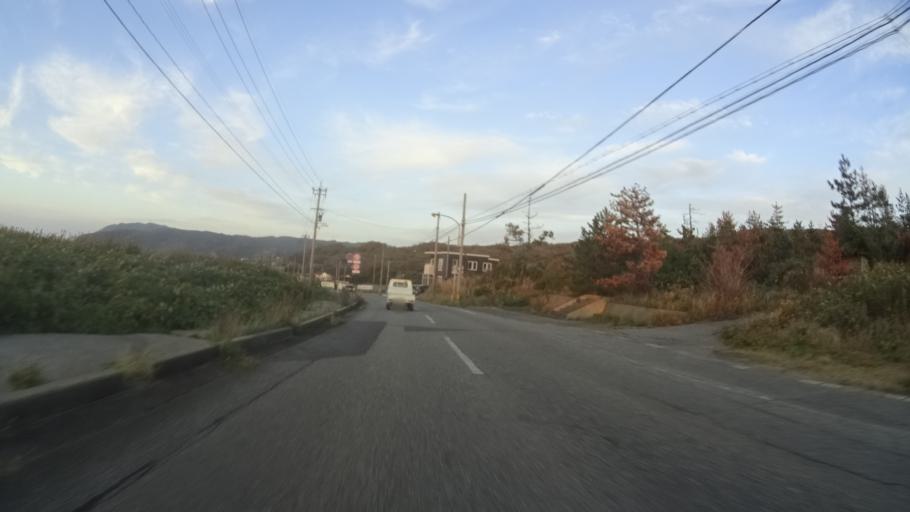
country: JP
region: Ishikawa
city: Nanao
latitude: 37.2715
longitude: 136.7310
